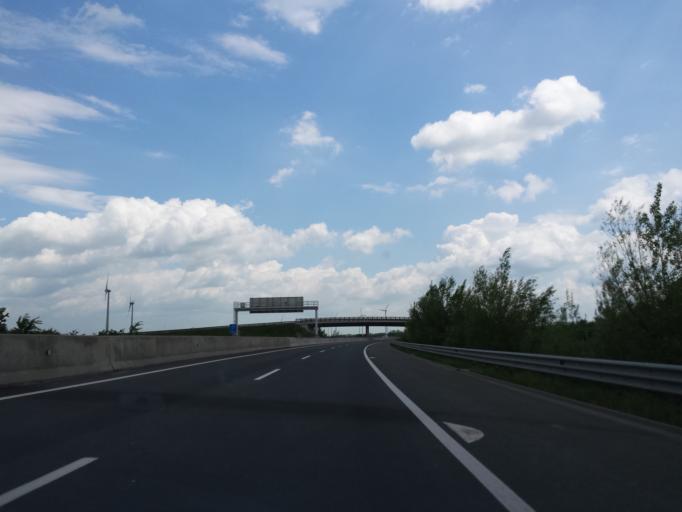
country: AT
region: Burgenland
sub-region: Politischer Bezirk Neusiedl am See
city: Parndorf
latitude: 48.0275
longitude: 16.8526
